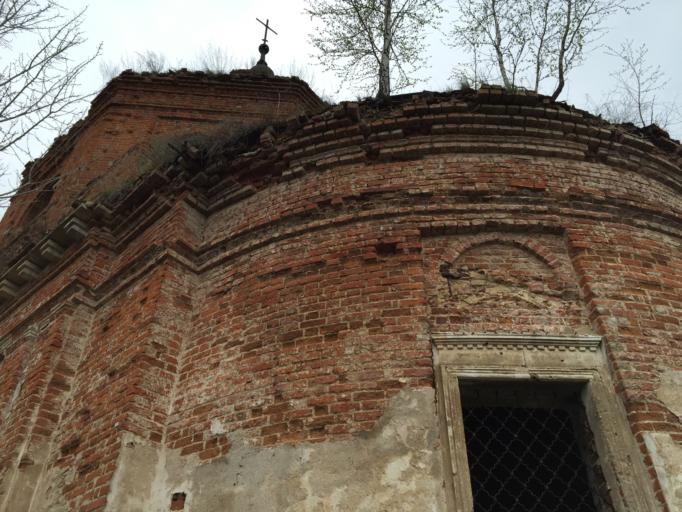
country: RU
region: Tula
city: Krapivna
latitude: 53.9437
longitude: 37.1501
